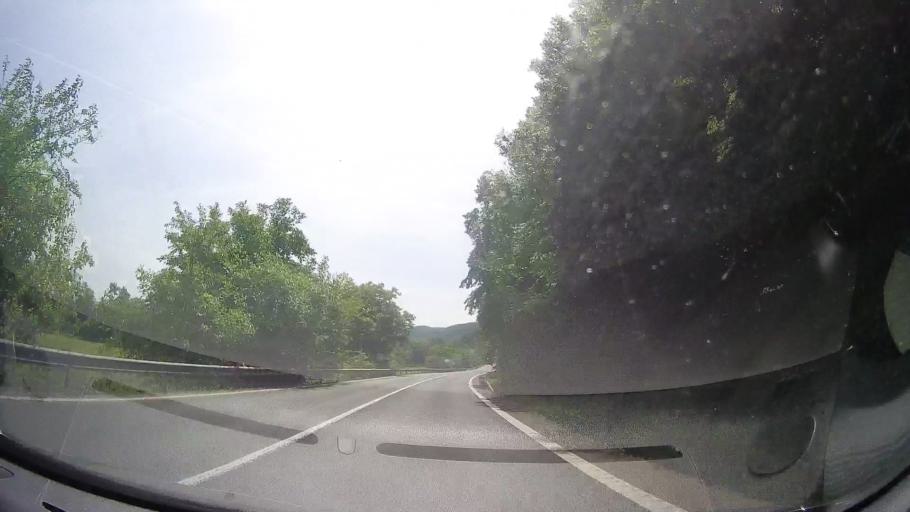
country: RO
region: Hunedoara
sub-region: Comuna Branisca
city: Branisca
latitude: 45.9131
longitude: 22.7670
